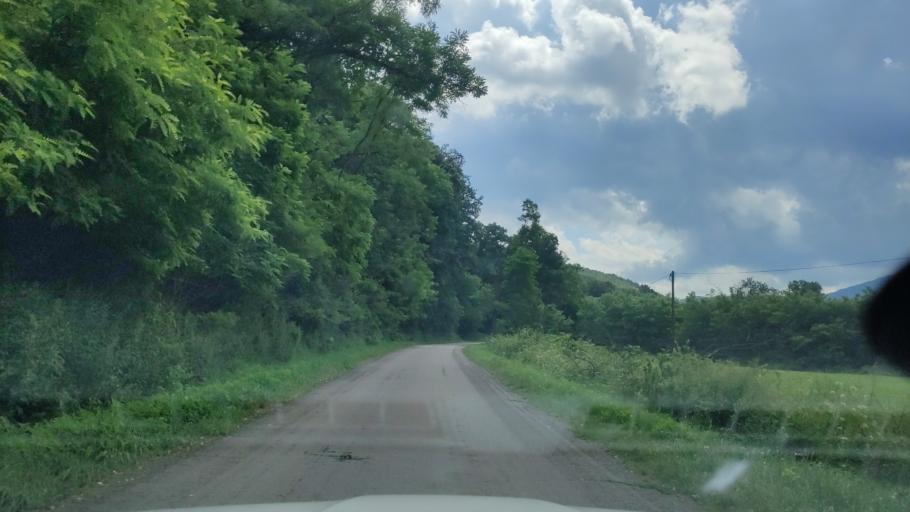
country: HU
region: Heves
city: Parad
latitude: 47.9176
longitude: 20.0584
